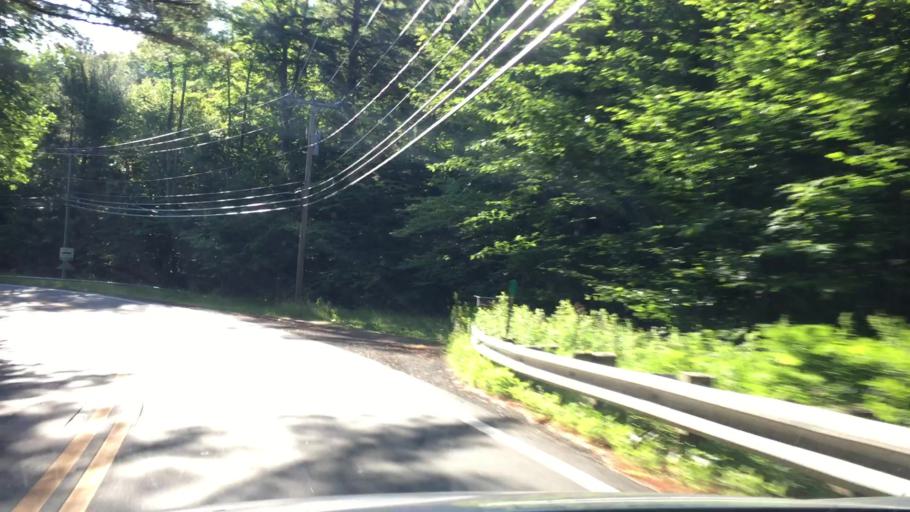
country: US
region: Massachusetts
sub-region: Berkshire County
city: Becket
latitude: 42.3196
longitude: -73.0889
